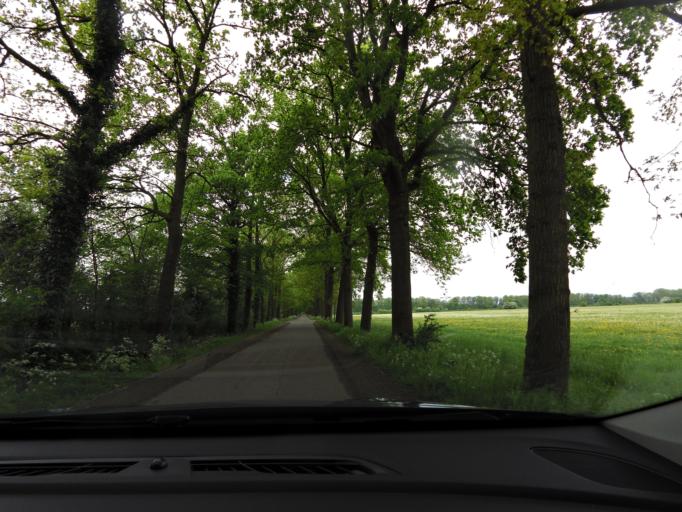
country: NL
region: Gelderland
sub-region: Gemeente Culemborg
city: Culemborg
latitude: 51.8904
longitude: 5.2169
